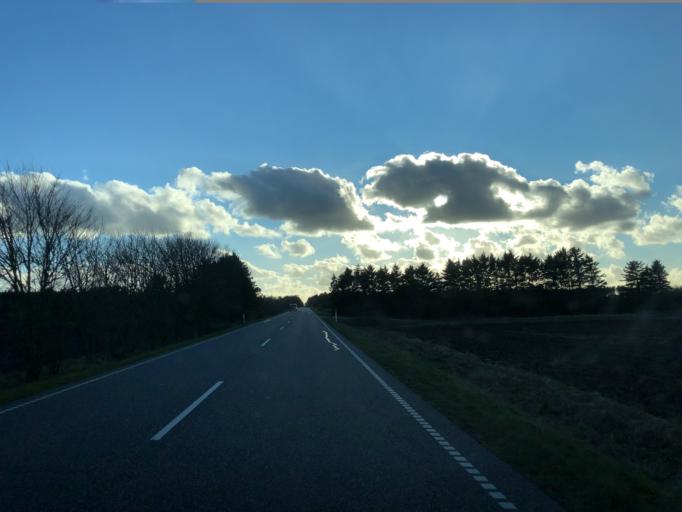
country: DK
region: Central Jutland
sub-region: Herning Kommune
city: Avlum
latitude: 56.2878
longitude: 8.8448
